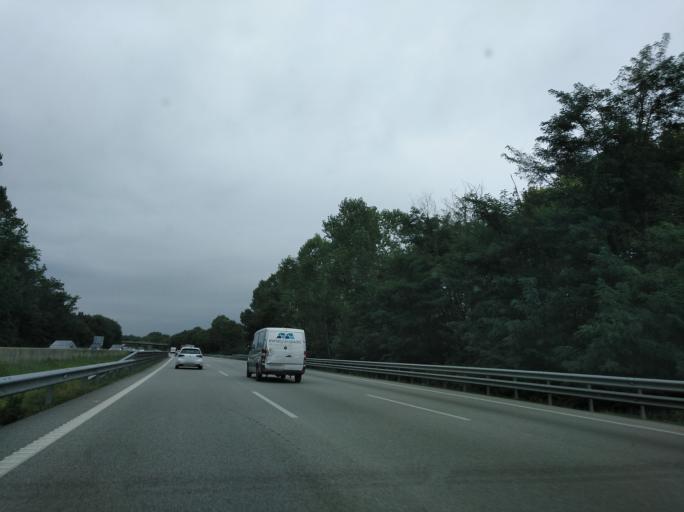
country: ES
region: Catalonia
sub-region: Provincia de Girona
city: Hostalric
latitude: 41.7294
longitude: 2.6165
